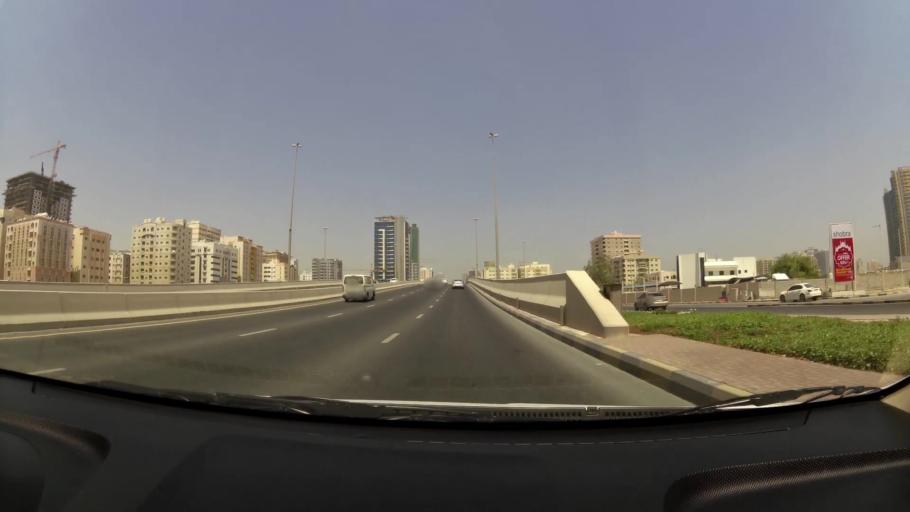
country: AE
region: Ajman
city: Ajman
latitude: 25.3897
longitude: 55.4565
